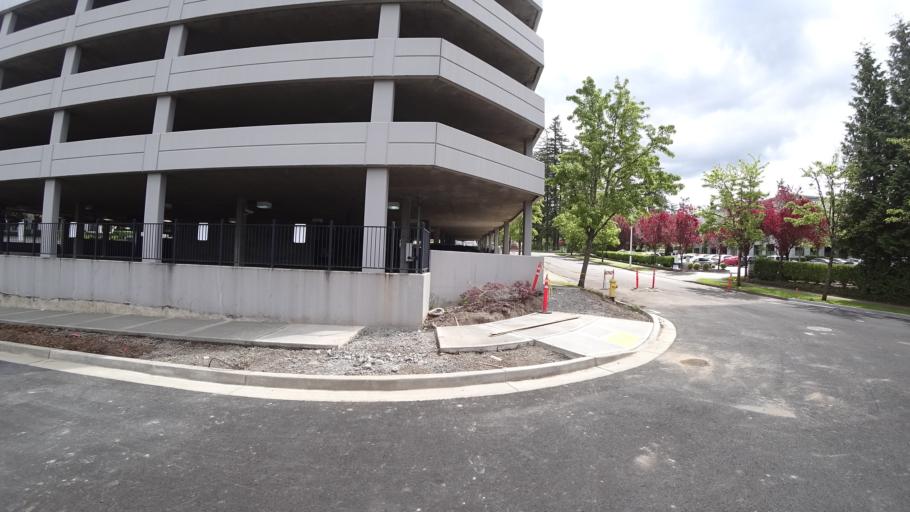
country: US
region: Oregon
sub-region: Washington County
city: Metzger
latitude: 45.4319
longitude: -122.7488
